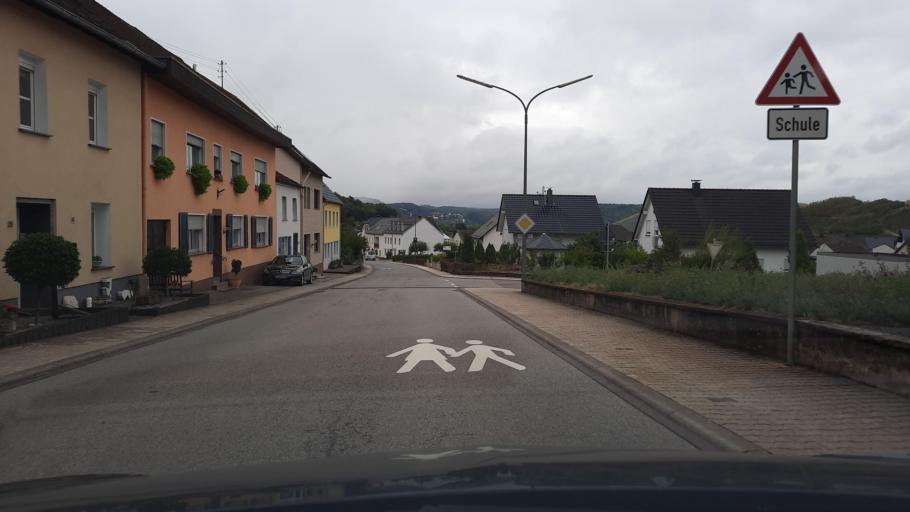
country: DE
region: Rheinland-Pfalz
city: Irsch
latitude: 49.6041
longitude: 6.5980
